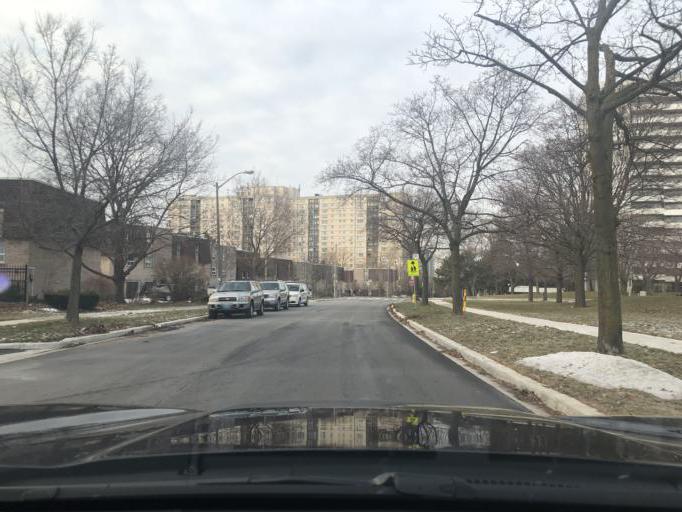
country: CA
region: Ontario
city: Willowdale
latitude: 43.7696
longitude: -79.3425
